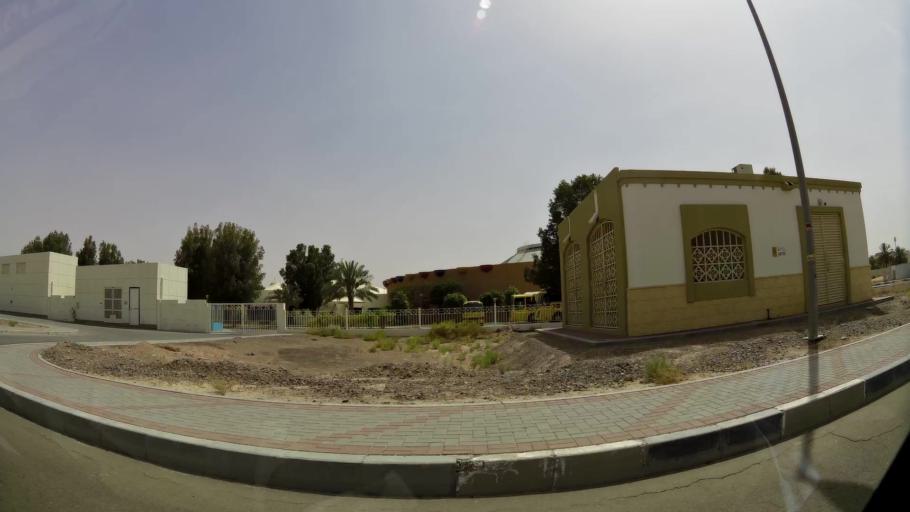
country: AE
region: Abu Dhabi
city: Al Ain
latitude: 24.1619
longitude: 55.6655
